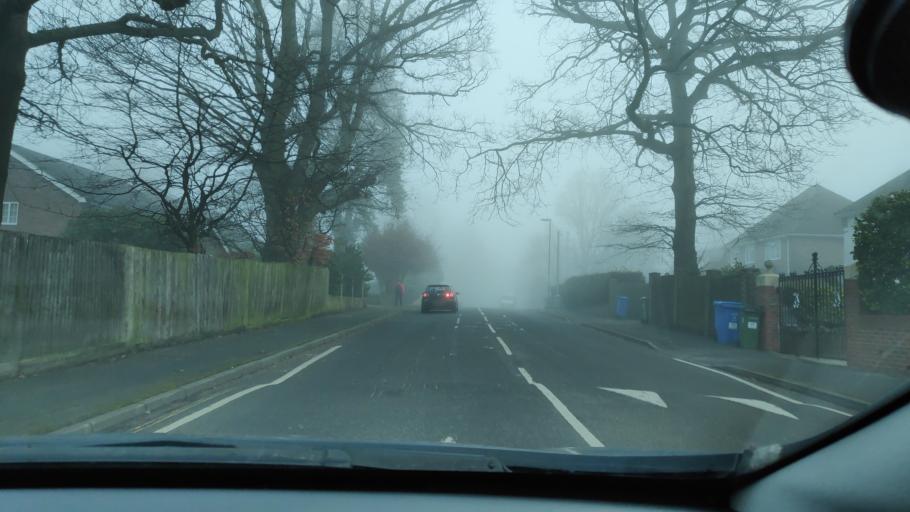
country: GB
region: England
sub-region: Hampshire
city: Farnborough
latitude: 51.2880
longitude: -0.7451
